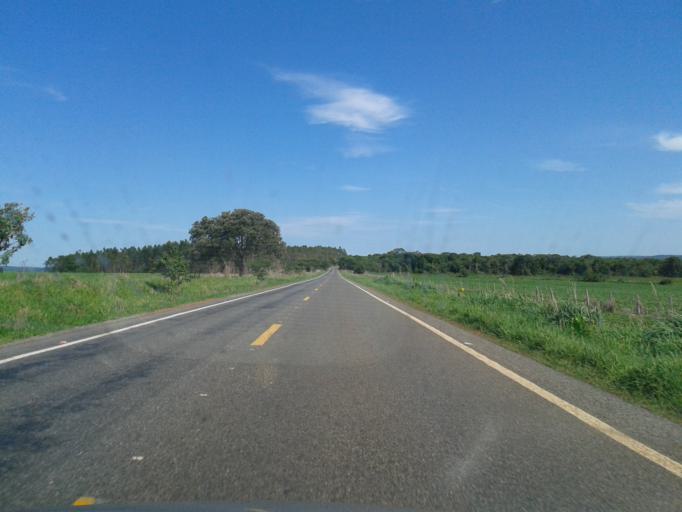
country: BR
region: Goias
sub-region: Piracanjuba
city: Piracanjuba
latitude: -17.3350
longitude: -48.7969
